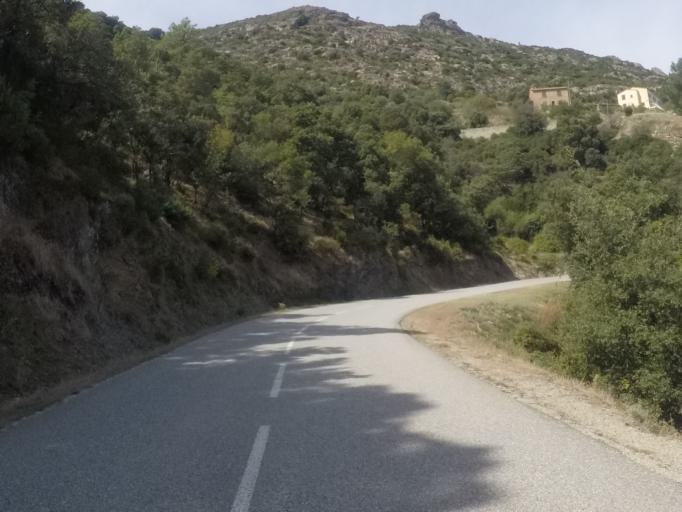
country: FR
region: Corsica
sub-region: Departement de la Haute-Corse
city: Corte
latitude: 42.3697
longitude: 9.1458
